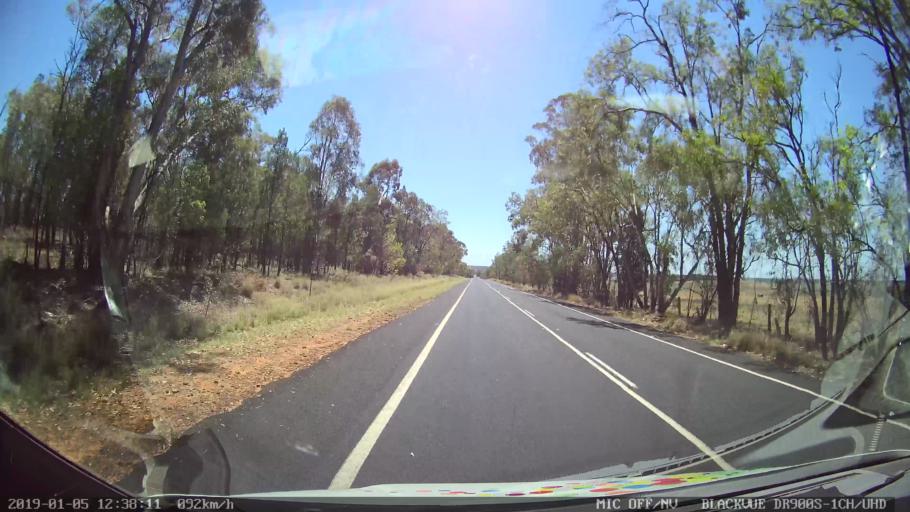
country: AU
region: New South Wales
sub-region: Warrumbungle Shire
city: Coonabarabran
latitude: -31.1976
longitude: 149.4649
